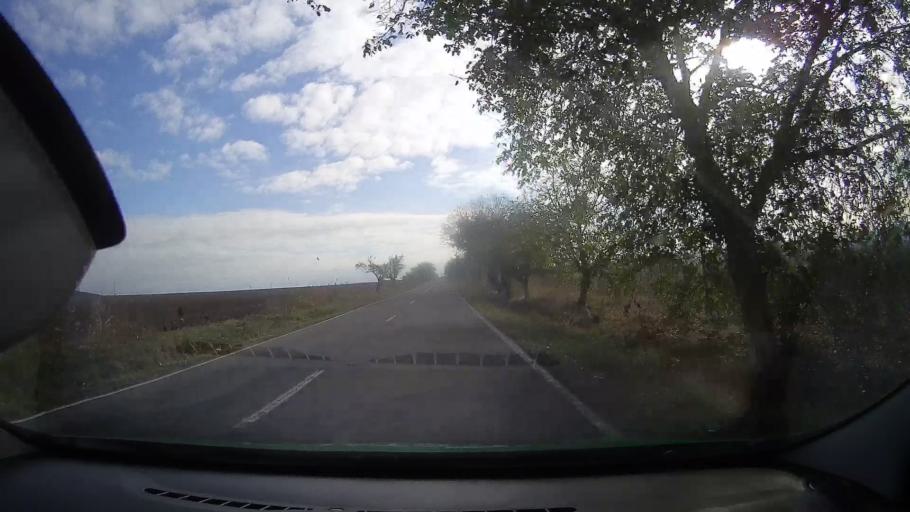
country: RO
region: Tulcea
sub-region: Comuna Bestepe
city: Bestepe
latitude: 45.0801
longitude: 29.0369
